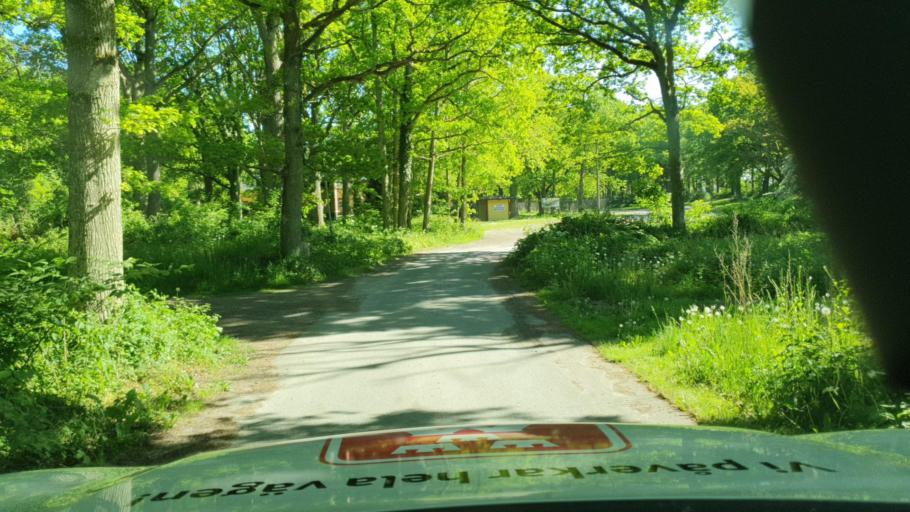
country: SE
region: Skane
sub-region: Simrishamns Kommun
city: Simrishamn
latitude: 55.4954
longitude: 14.2755
